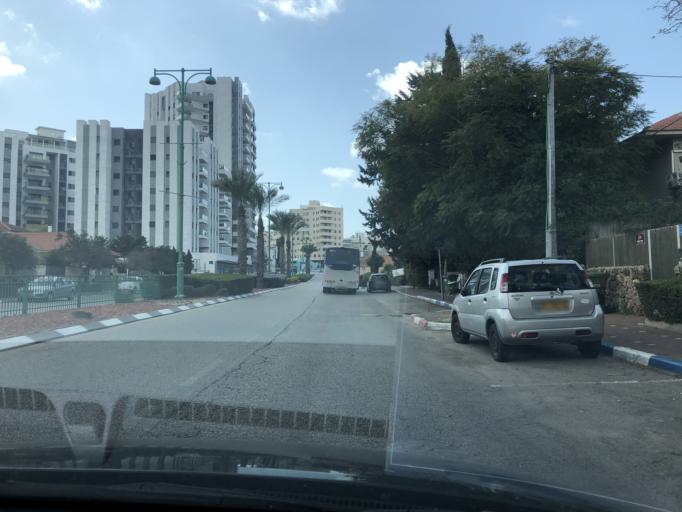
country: IL
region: Haifa
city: Hadera
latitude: 32.4389
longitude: 34.9291
